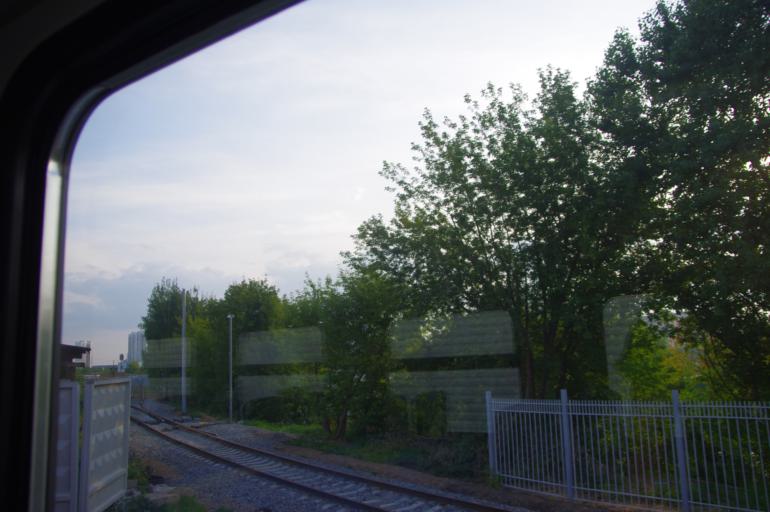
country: RU
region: Moscow
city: Solntsevo
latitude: 55.6509
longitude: 37.3804
